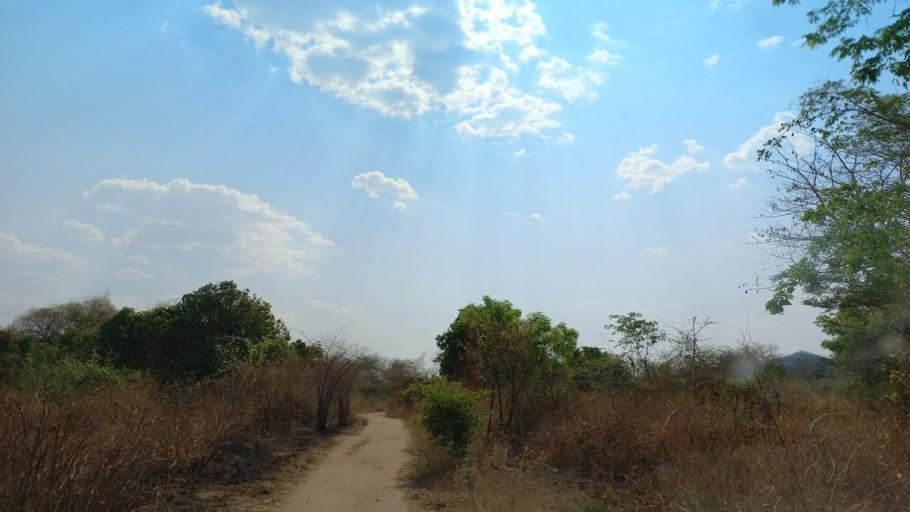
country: ZM
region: Lusaka
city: Luangwa
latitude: -15.0909
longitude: 30.1526
